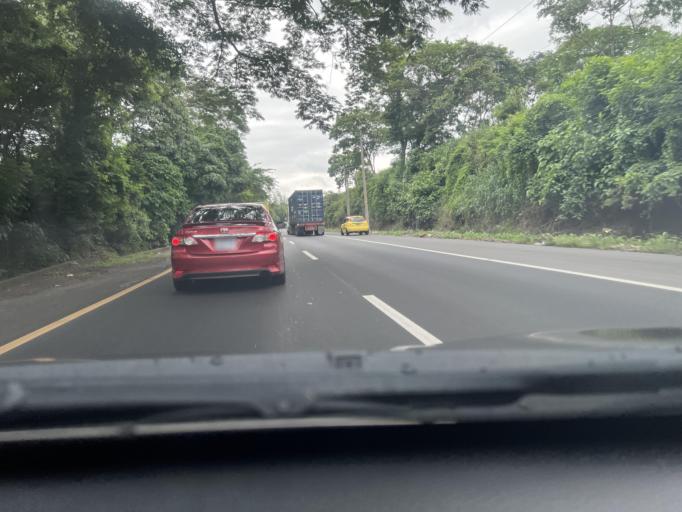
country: SV
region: Santa Ana
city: El Congo
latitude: 13.8792
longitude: -89.4901
